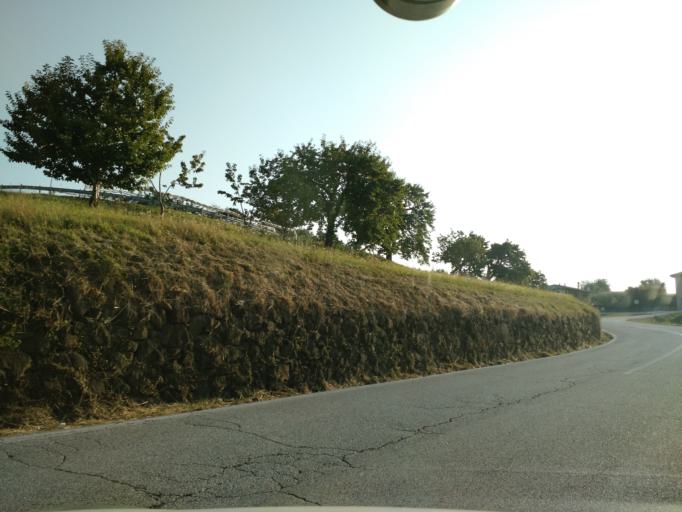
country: IT
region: Veneto
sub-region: Provincia di Vicenza
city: Salcedo
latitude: 45.7640
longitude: 11.5654
